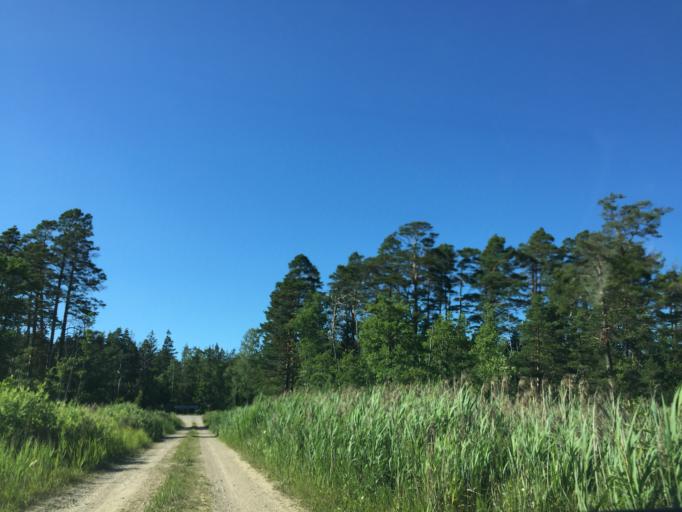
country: LV
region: Ventspils
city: Ventspils
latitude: 57.5549
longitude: 21.7590
